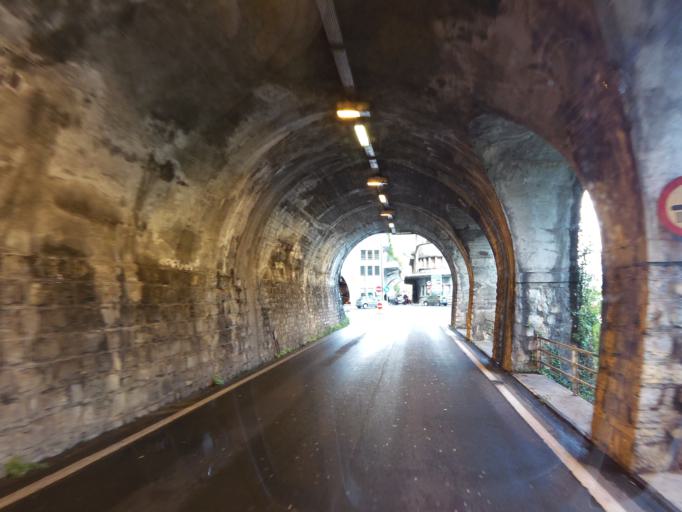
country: IT
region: Lombardy
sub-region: Provincia di Como
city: San Mamete
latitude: 46.0182
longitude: 9.0247
